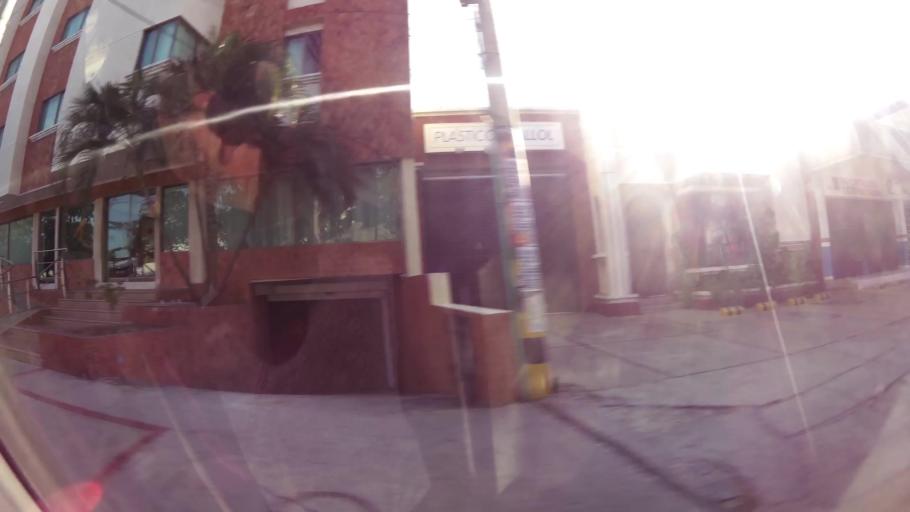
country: CO
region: Atlantico
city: Barranquilla
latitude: 10.9962
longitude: -74.8092
